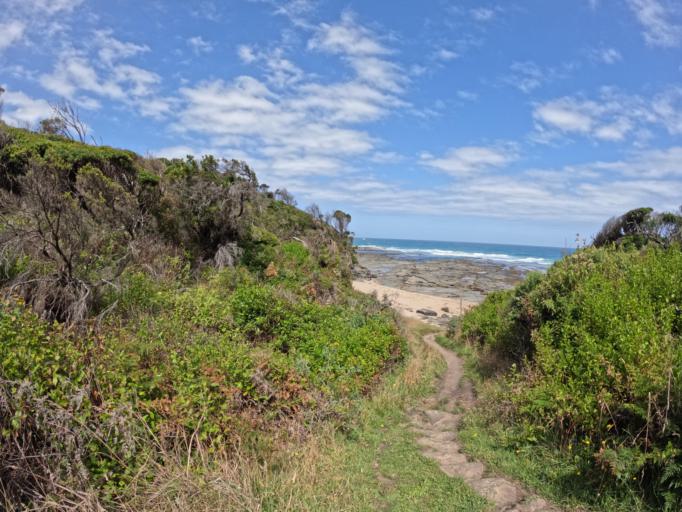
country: AU
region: Victoria
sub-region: Colac-Otway
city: Apollo Bay
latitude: -38.7922
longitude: 143.6232
